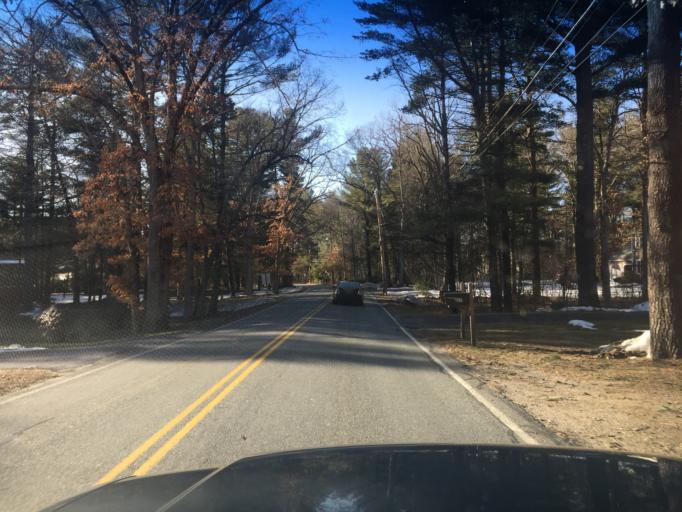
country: US
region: Massachusetts
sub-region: Norfolk County
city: Bellingham
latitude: 42.0924
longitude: -71.5142
